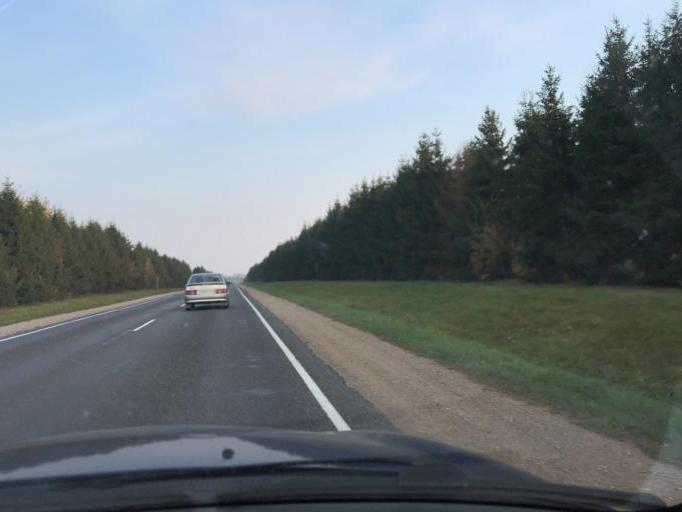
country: BY
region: Grodnenskaya
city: Karelichy
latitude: 53.5915
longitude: 26.0869
